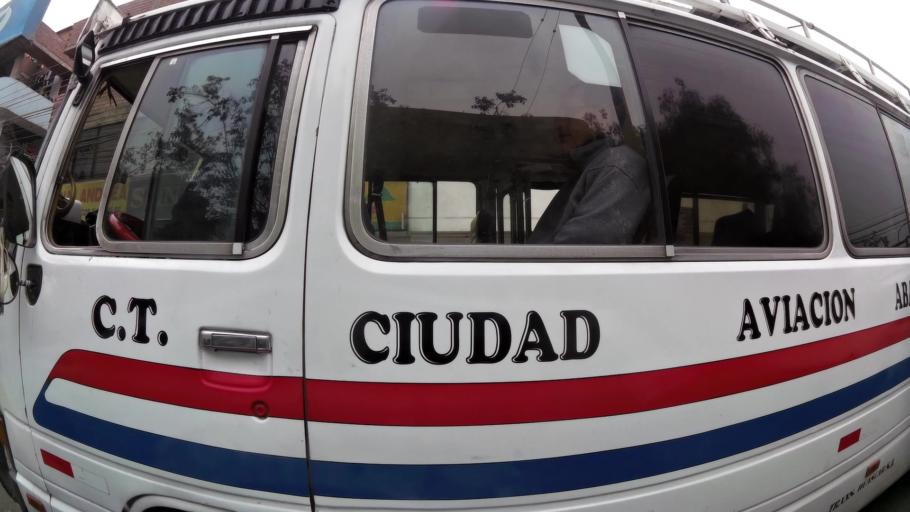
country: PE
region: Lima
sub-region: Lima
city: Independencia
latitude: -11.9473
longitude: -76.9855
